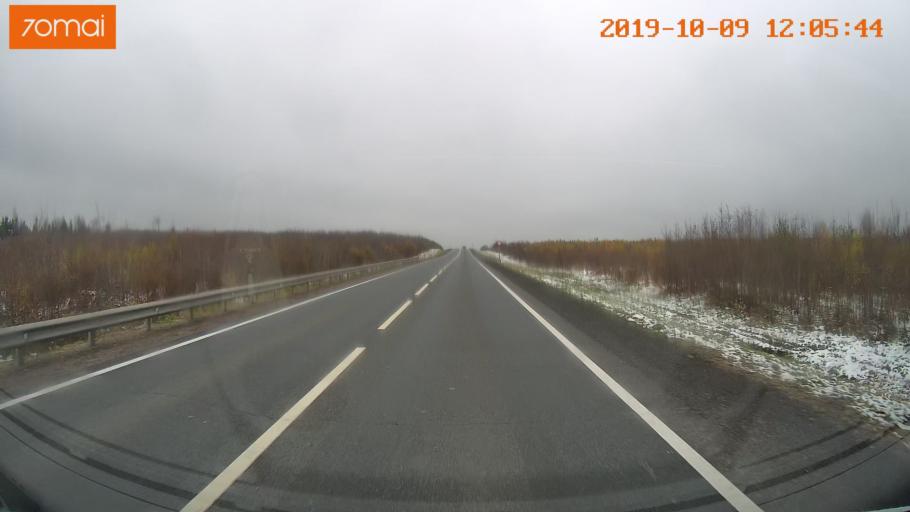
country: RU
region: Jaroslavl
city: Prechistoye
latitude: 58.6252
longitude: 40.3304
